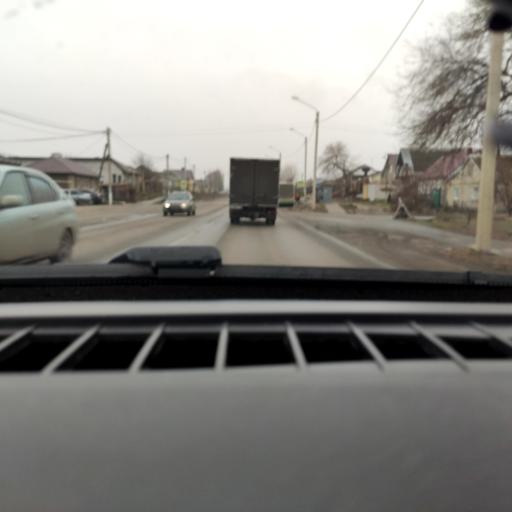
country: RU
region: Voronezj
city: Pridonskoy
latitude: 51.7122
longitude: 39.0744
